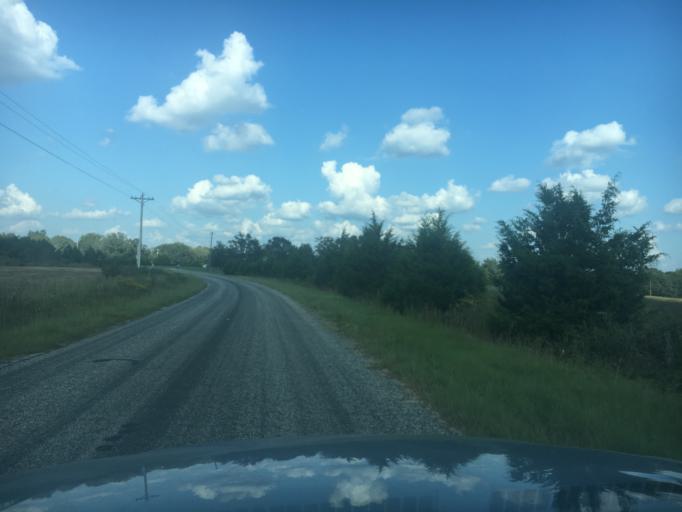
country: US
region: South Carolina
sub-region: Greenwood County
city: Ware Shoals
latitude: 34.4874
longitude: -82.2325
